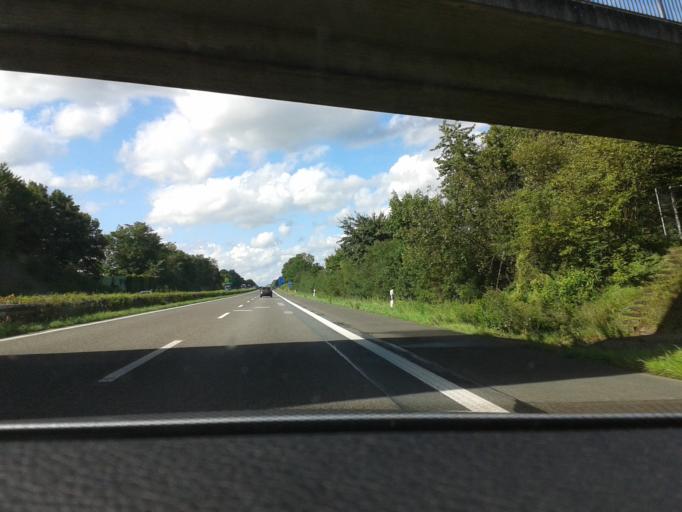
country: DE
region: North Rhine-Westphalia
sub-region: Regierungsbezirk Dusseldorf
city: Sonsbeck
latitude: 51.5973
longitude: 6.3628
